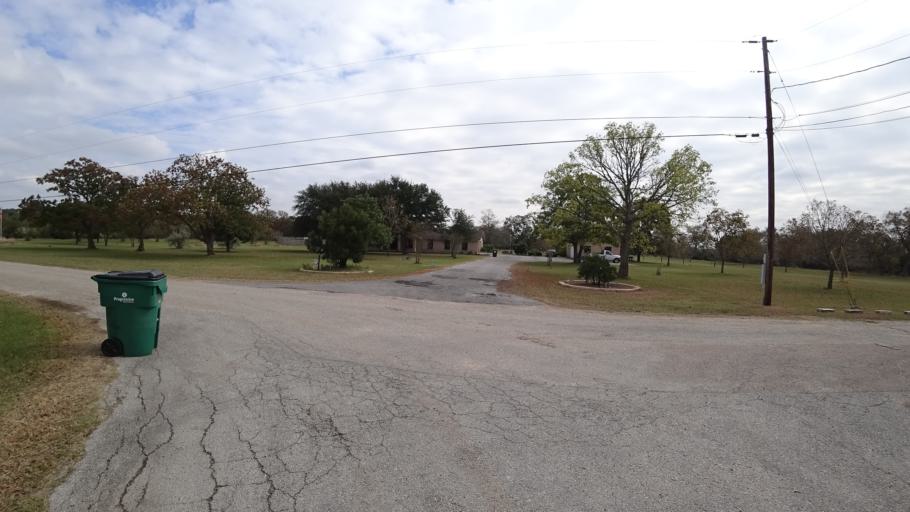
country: US
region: Texas
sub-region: Travis County
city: Shady Hollow
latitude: 30.2076
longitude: -97.8991
